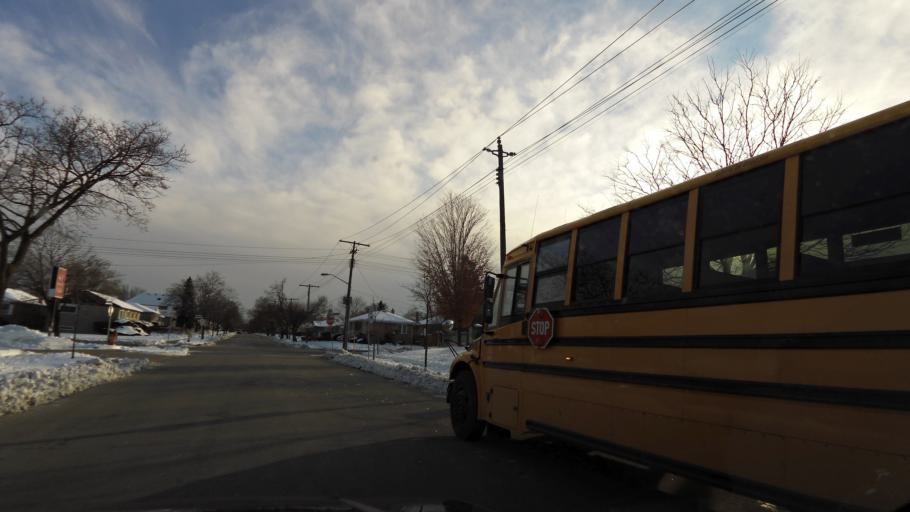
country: CA
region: Ontario
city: Etobicoke
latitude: 43.6668
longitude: -79.5792
